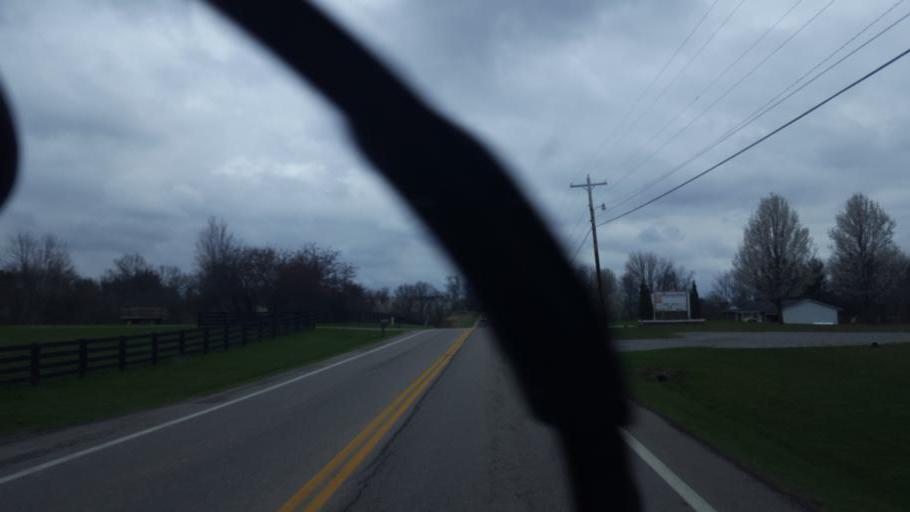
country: US
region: Ohio
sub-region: Delaware County
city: Sunbury
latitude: 40.2740
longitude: -82.8513
